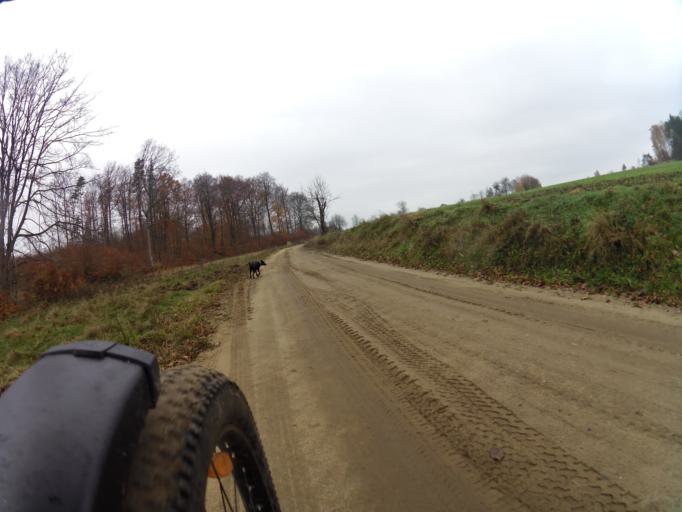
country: PL
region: Pomeranian Voivodeship
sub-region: Powiat pucki
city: Krokowa
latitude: 54.7154
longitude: 18.1394
